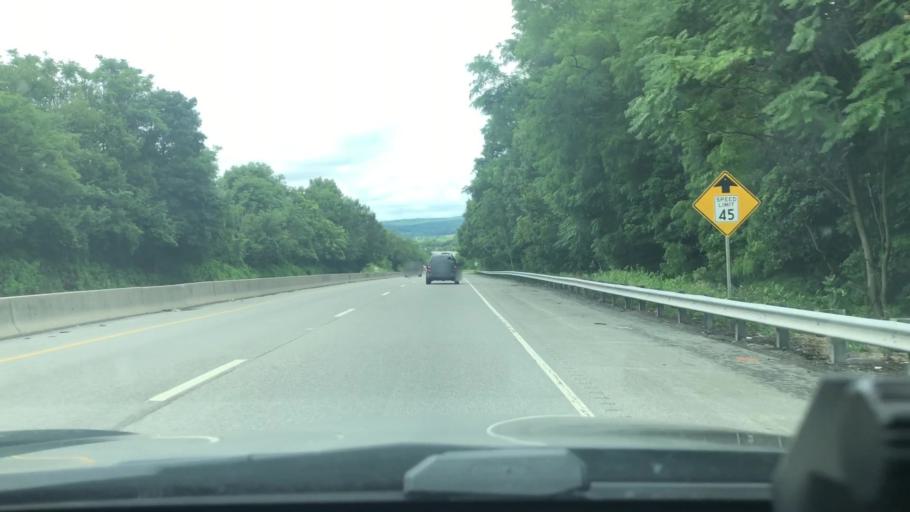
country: US
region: Pennsylvania
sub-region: Montgomery County
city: Pottstown
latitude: 40.2610
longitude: -75.6535
